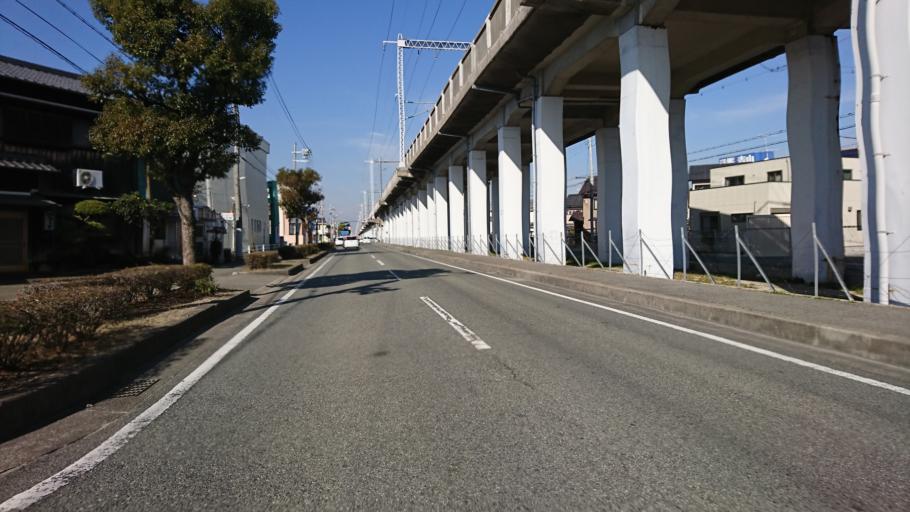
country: JP
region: Hyogo
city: Kakogawacho-honmachi
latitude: 34.7657
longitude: 134.8003
